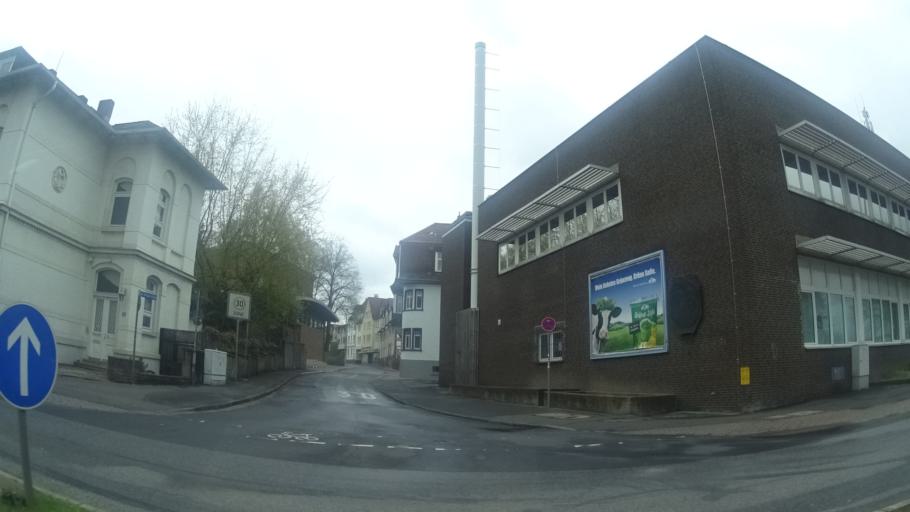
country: DE
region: Hesse
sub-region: Regierungsbezirk Kassel
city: Bad Hersfeld
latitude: 50.8660
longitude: 9.7110
